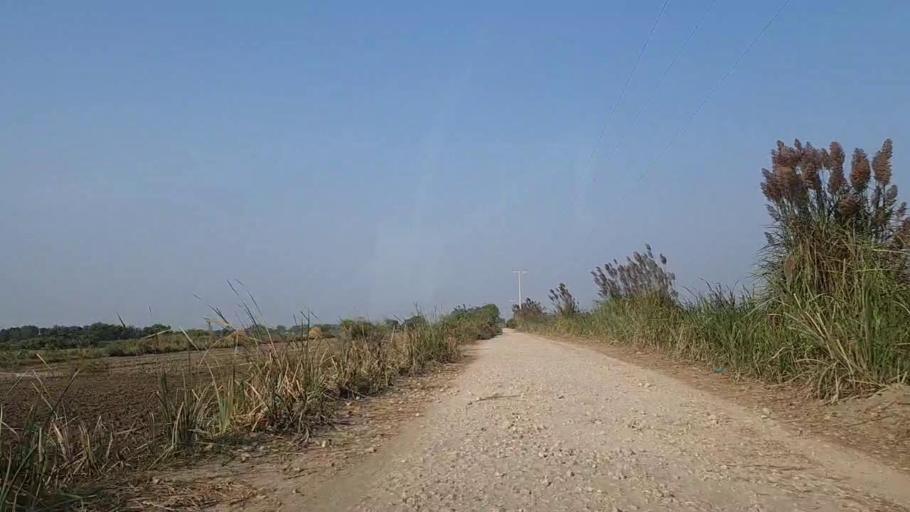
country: PK
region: Sindh
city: Mirpur Sakro
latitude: 24.6286
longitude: 67.7460
